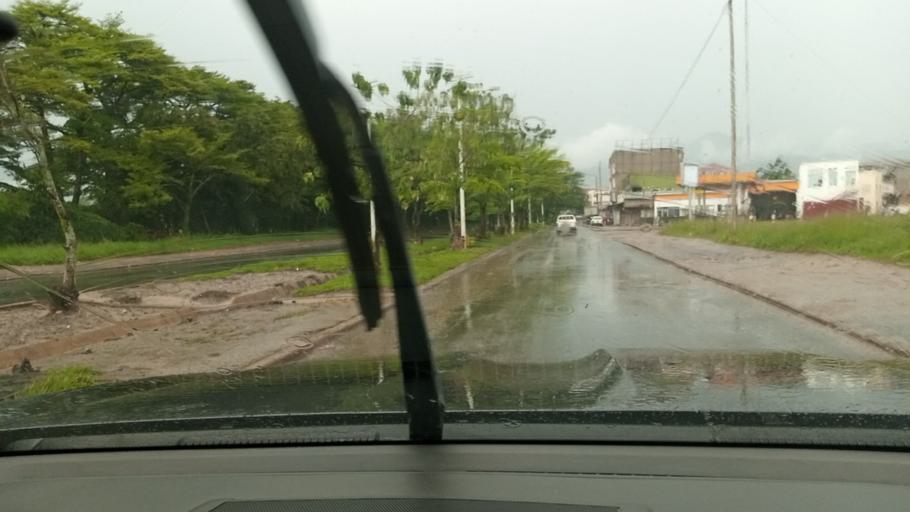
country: BI
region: Bujumbura Mairie
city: Bujumbura
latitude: -3.3795
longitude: 29.3550
